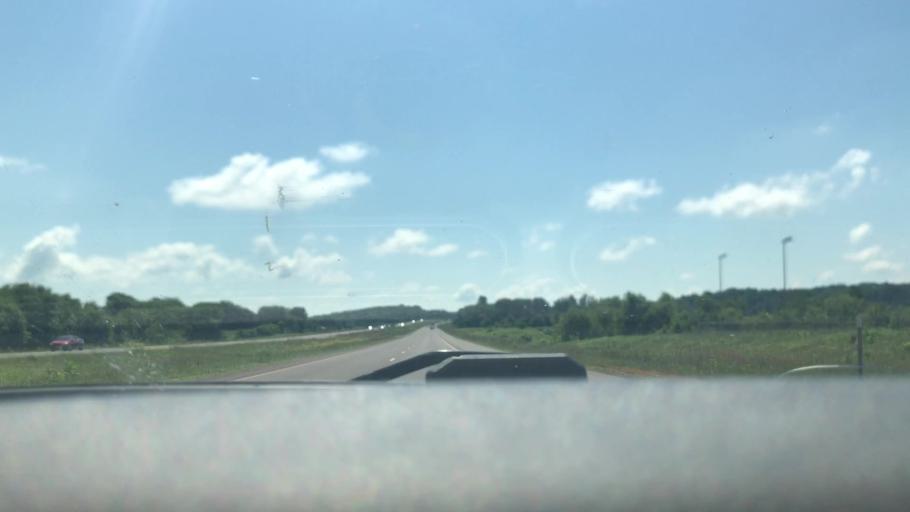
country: US
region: Wisconsin
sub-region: Chippewa County
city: Bloomer
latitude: 45.0961
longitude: -91.4992
